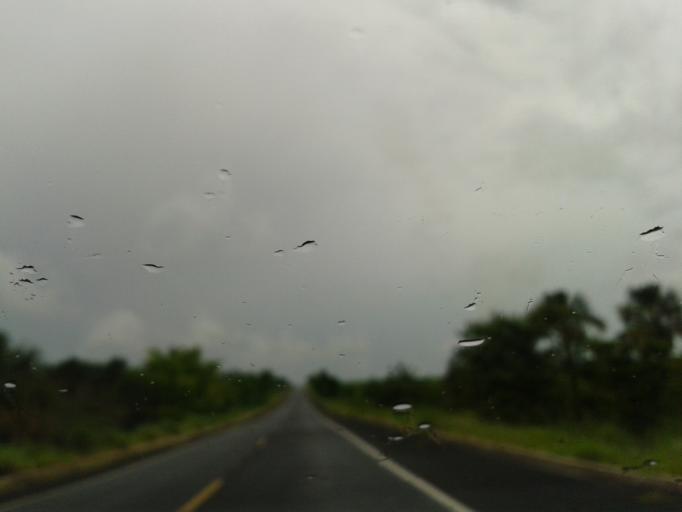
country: BR
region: Minas Gerais
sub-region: Santa Vitoria
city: Santa Vitoria
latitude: -19.1505
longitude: -50.1543
